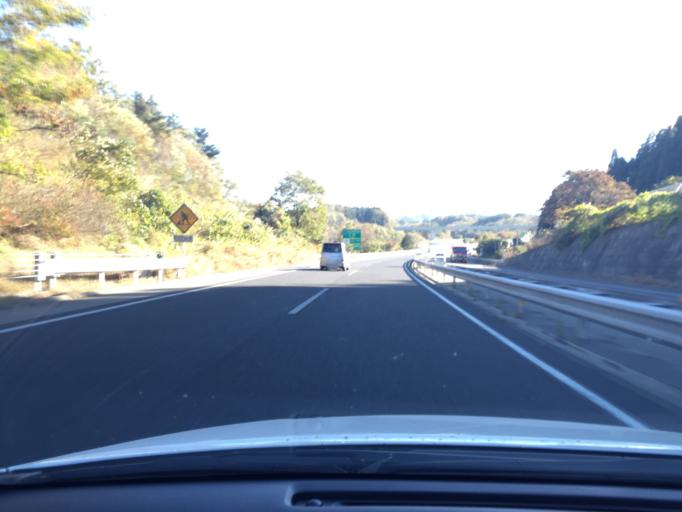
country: JP
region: Fukushima
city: Funehikimachi-funehiki
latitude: 37.3016
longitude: 140.6147
